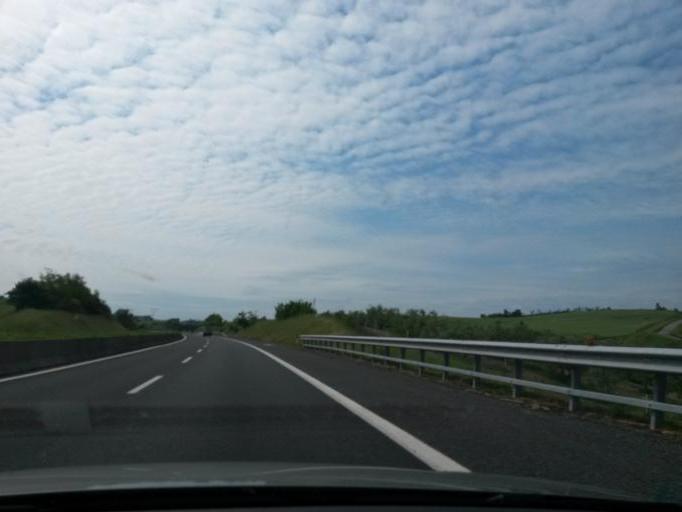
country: IT
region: Tuscany
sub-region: Provincia di Livorno
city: Collesalvetti
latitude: 43.5359
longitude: 10.4659
